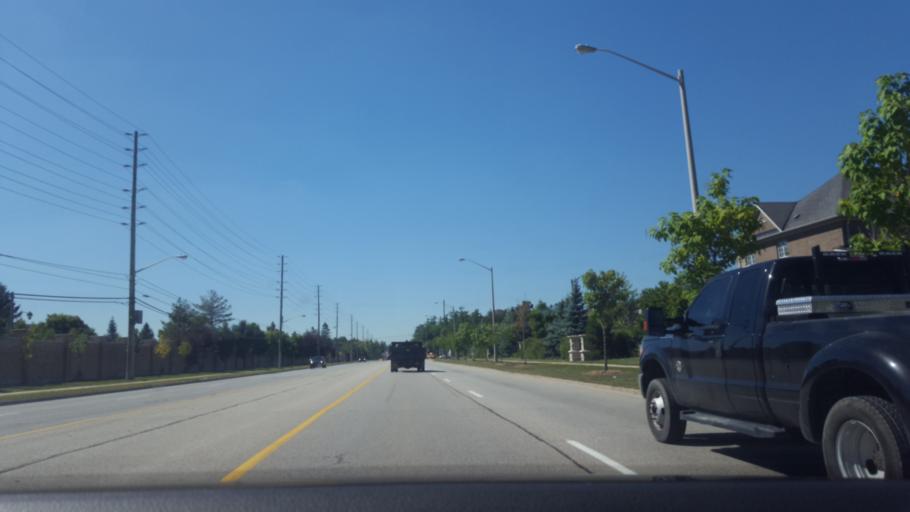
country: CA
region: Ontario
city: Vaughan
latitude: 43.8228
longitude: -79.5732
